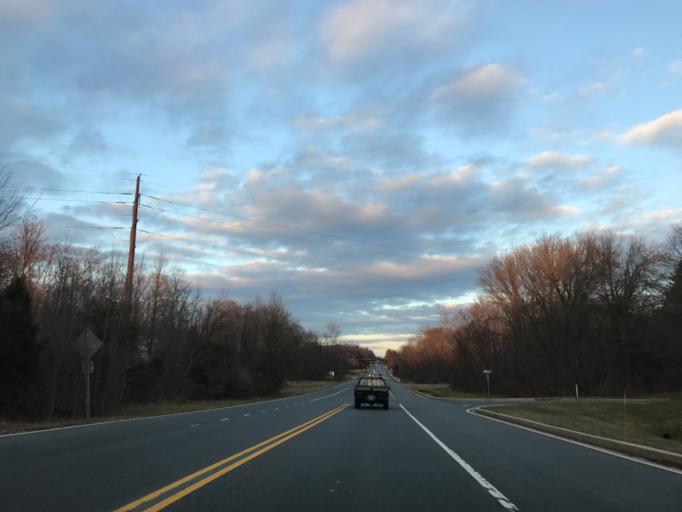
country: US
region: Maryland
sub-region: Cecil County
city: Elkton
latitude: 39.6100
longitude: -75.8519
